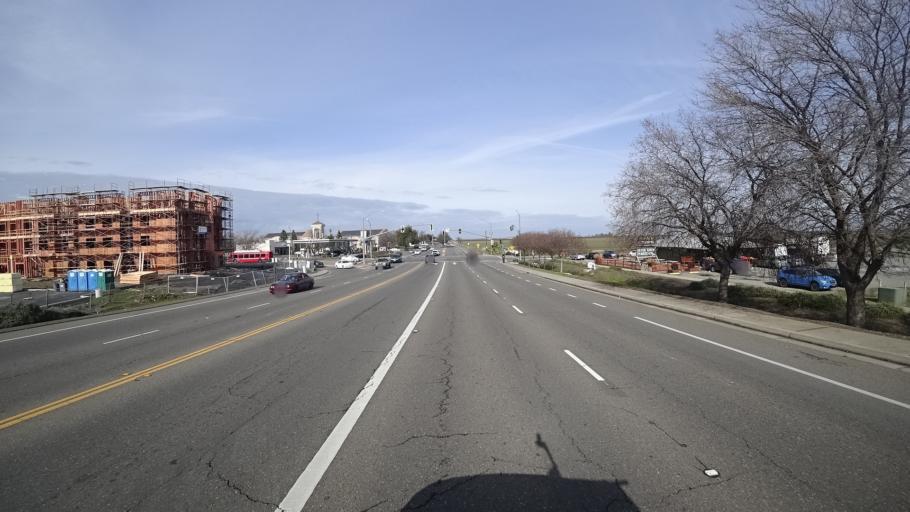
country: US
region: California
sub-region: Yolo County
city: Davis
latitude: 38.5555
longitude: -121.6942
